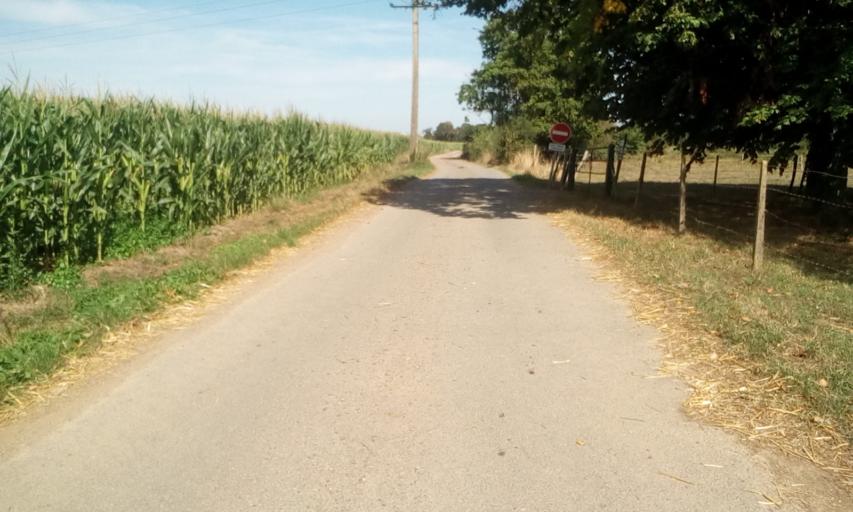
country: FR
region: Lower Normandy
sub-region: Departement du Calvados
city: Fontaine-Etoupefour
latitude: 49.1391
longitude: -0.4440
